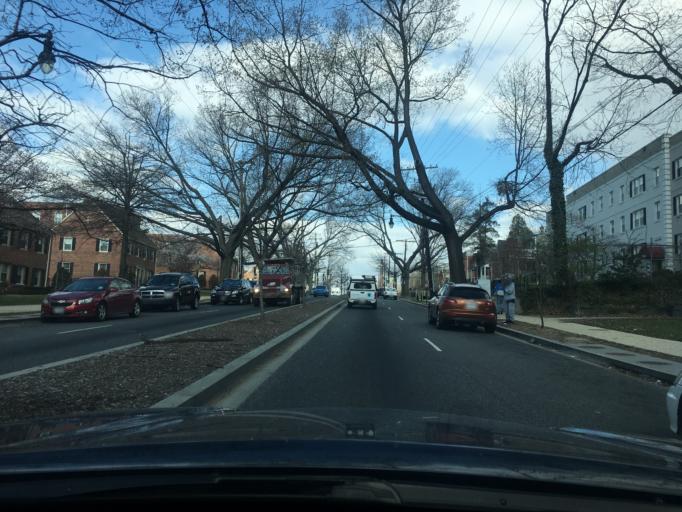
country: US
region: Maryland
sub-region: Prince George's County
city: Silver Hill
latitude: 38.8643
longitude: -76.9482
